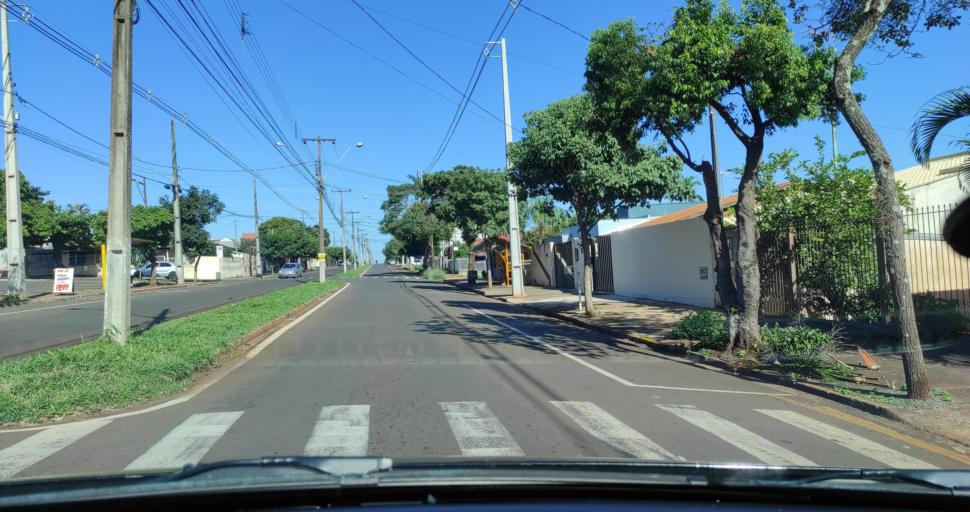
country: BR
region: Parana
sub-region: Ibipora
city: Ibipora
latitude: -23.2705
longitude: -51.0592
